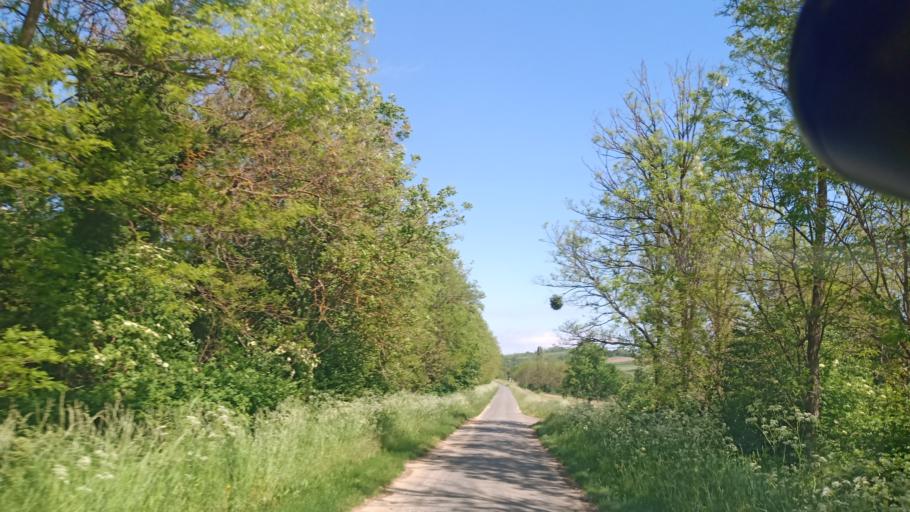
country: HU
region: Zala
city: Pacsa
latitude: 46.6414
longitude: 17.0622
